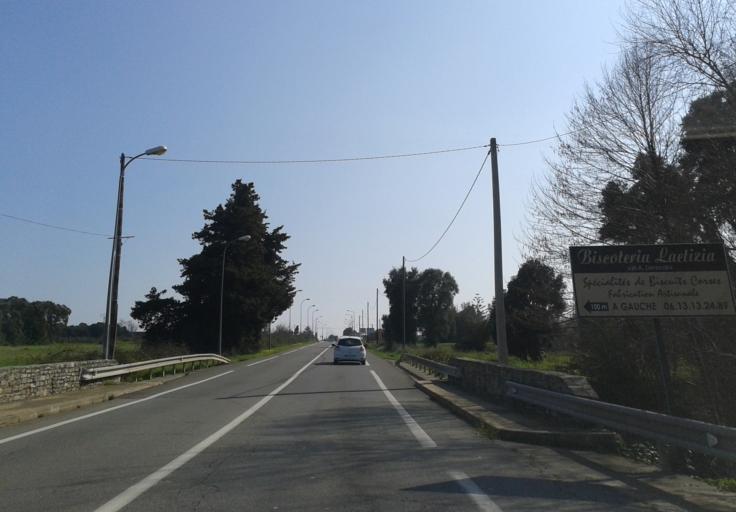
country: FR
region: Corsica
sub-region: Departement de la Haute-Corse
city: Cervione
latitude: 42.3233
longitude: 9.5392
